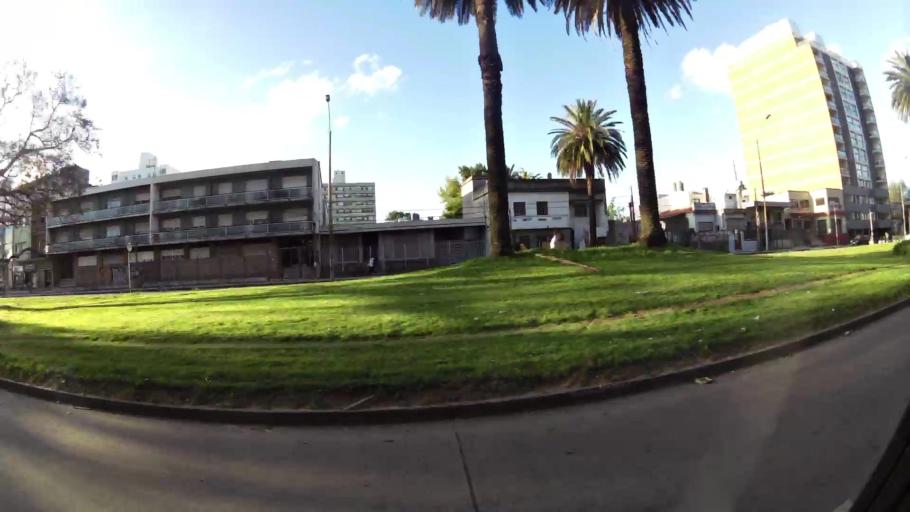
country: UY
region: Montevideo
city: Montevideo
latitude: -34.8885
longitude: -56.1465
